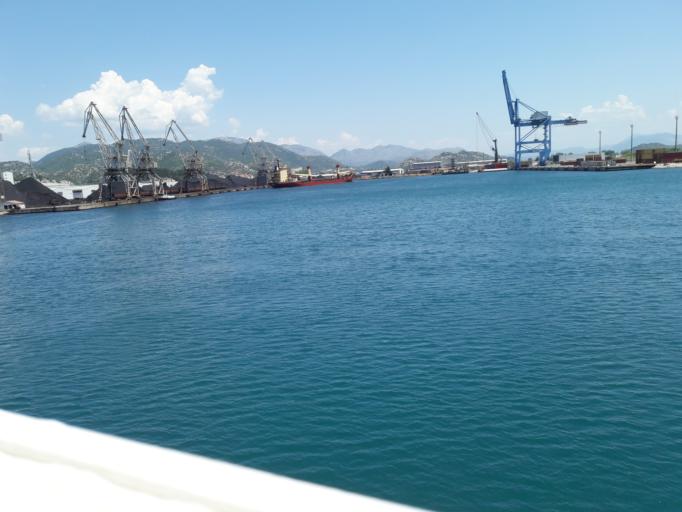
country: HR
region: Dubrovacko-Neretvanska
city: Komin
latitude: 43.0448
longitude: 17.4215
